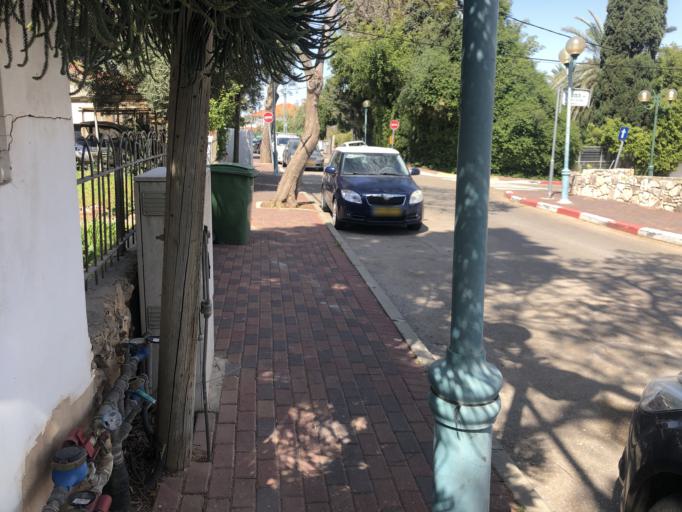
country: IL
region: Central District
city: Kfar Saba
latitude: 32.1600
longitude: 34.9226
